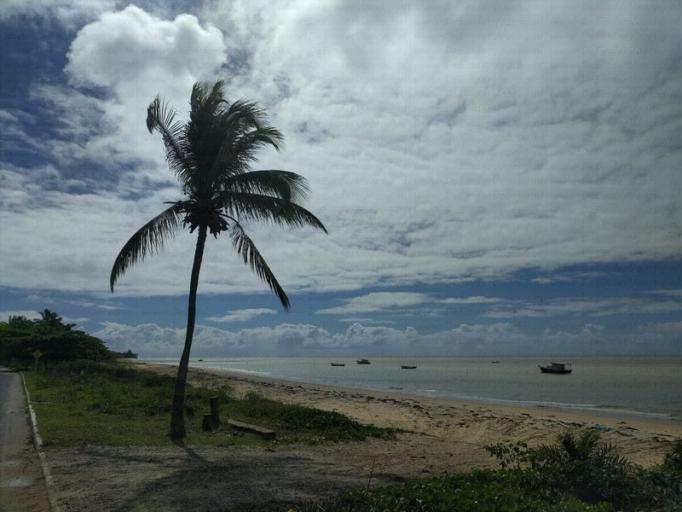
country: BR
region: Bahia
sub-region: Nova Vicosa
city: Nova Vicosa
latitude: -17.7322
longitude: -39.1840
